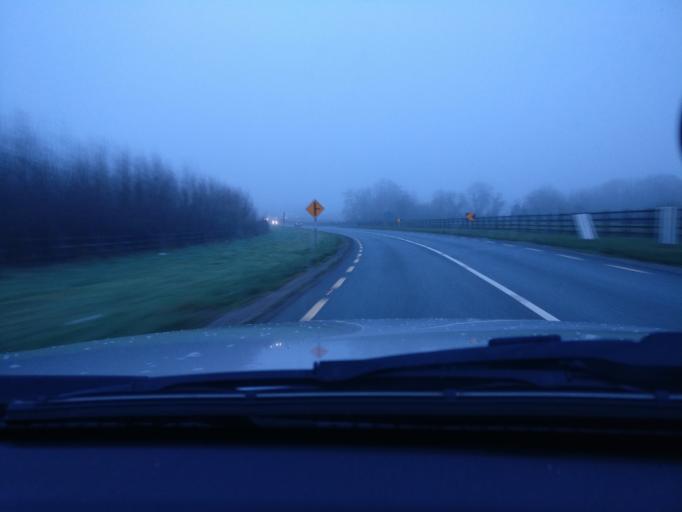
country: IE
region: Leinster
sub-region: An Mhi
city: Athboy
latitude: 53.6342
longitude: -6.8951
